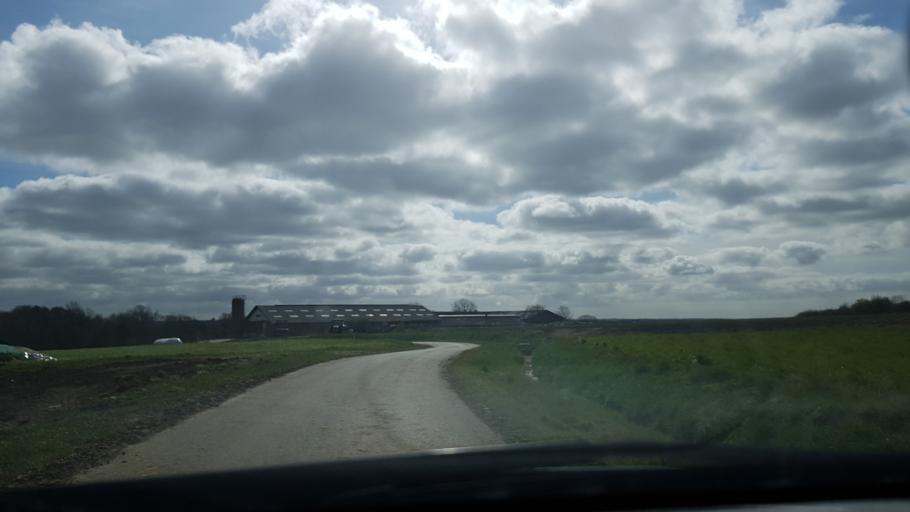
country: DK
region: South Denmark
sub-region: Haderslev Kommune
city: Gram
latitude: 55.3220
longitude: 8.9880
